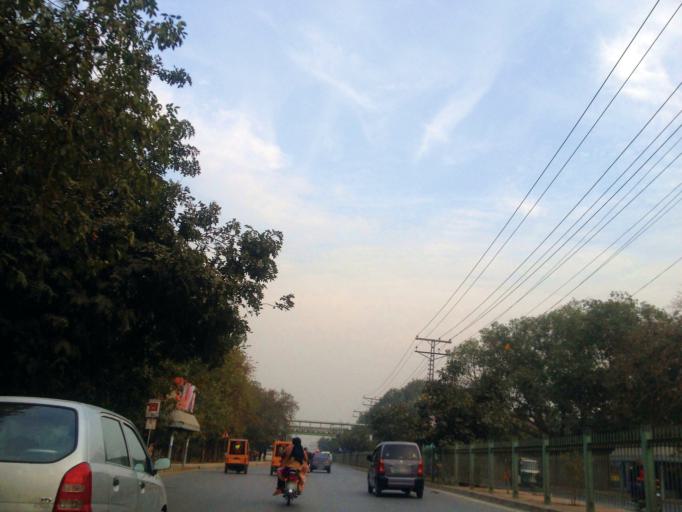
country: PK
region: Punjab
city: Lahore
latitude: 31.5085
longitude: 74.3056
